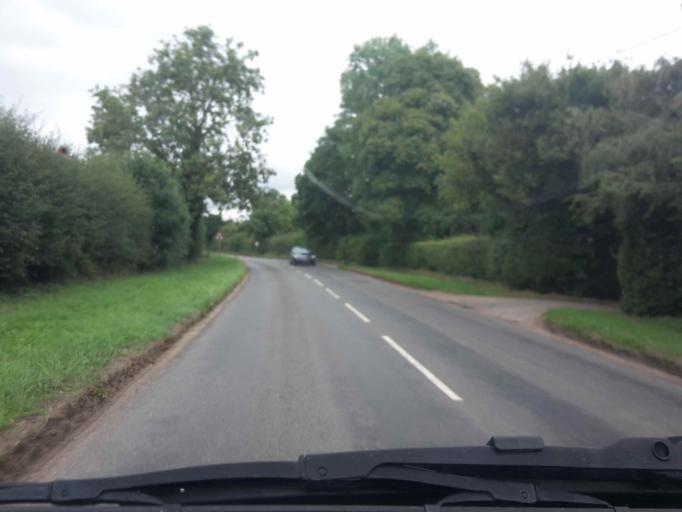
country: GB
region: England
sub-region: Oxfordshire
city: Rotherfield Peppard
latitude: 51.5352
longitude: -0.9770
